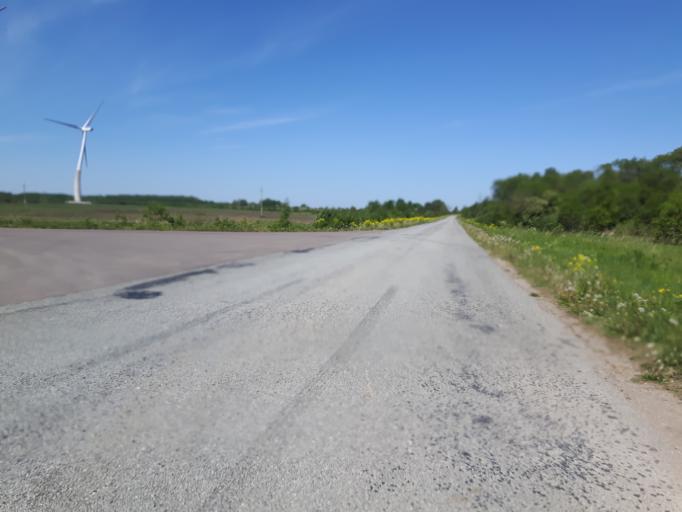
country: EE
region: Ida-Virumaa
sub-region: Aseri vald
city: Aseri
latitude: 59.4611
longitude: 26.8319
